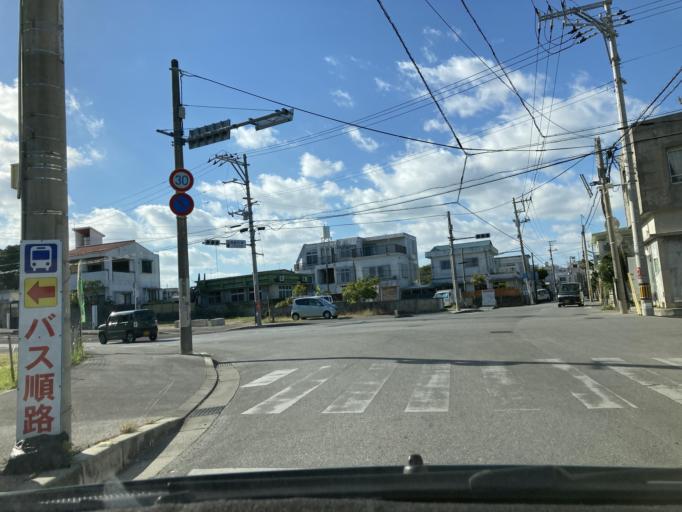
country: JP
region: Okinawa
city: Katsuren-haebaru
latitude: 26.3219
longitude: 127.9112
